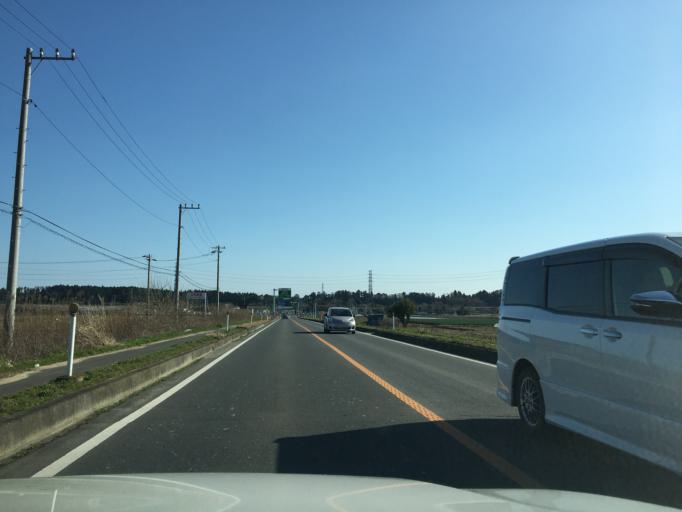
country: JP
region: Ibaraki
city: Mito-shi
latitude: 36.4223
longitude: 140.4228
